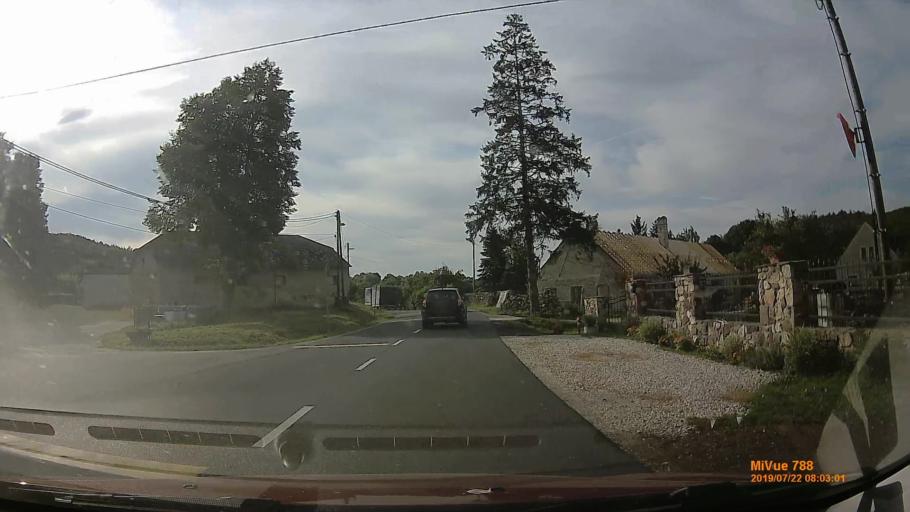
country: HU
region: Veszprem
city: Urkut
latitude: 46.9989
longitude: 17.6496
